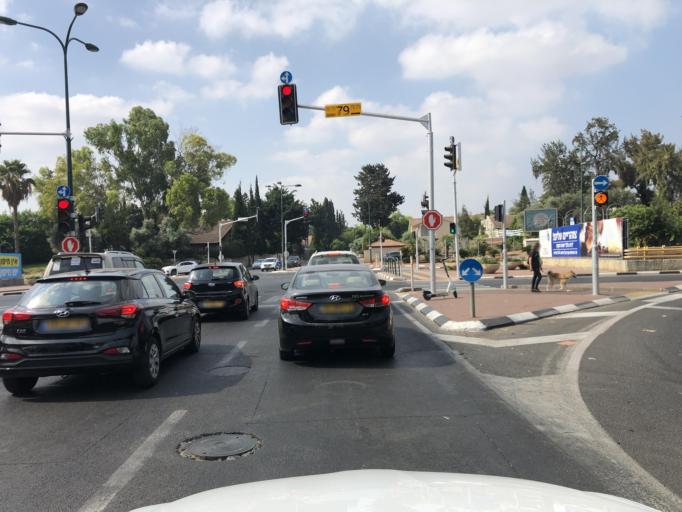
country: IL
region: Tel Aviv
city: Giv`atayim
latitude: 32.0592
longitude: 34.8281
